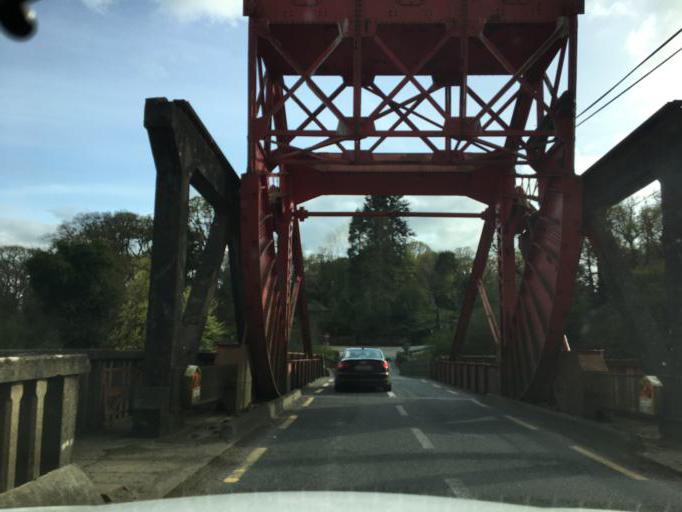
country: IE
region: Leinster
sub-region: Loch Garman
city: New Ross
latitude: 52.4206
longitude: -6.9342
